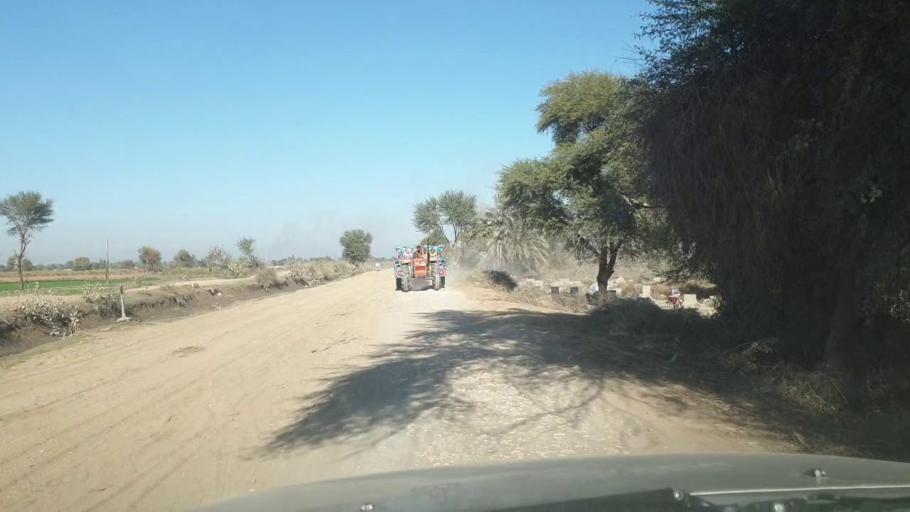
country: PK
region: Sindh
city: Ghotki
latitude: 28.0773
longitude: 69.3463
